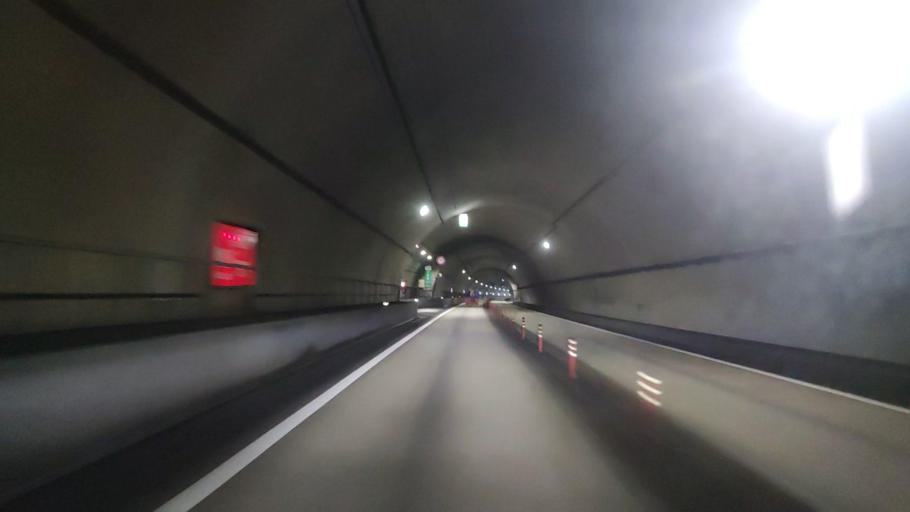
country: JP
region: Wakayama
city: Tanabe
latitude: 33.5494
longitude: 135.5163
